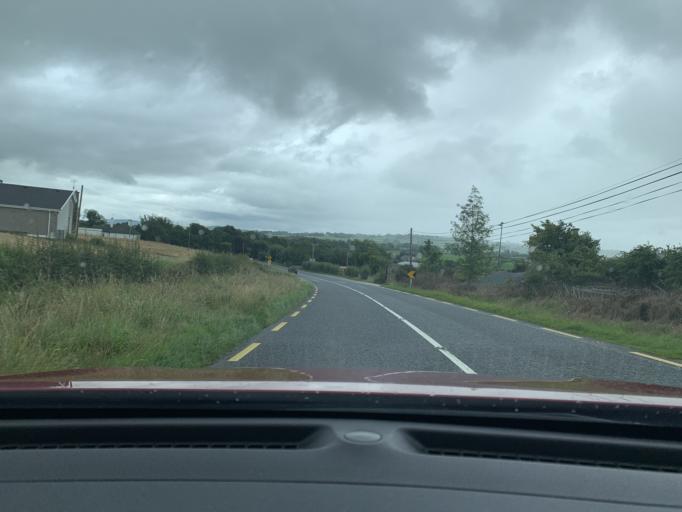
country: IE
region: Ulster
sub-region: County Donegal
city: Leifear
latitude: 54.7936
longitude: -7.5557
